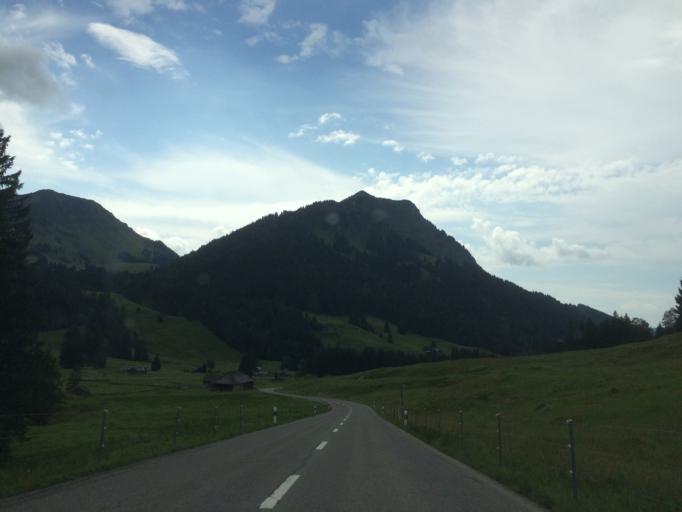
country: CH
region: Appenzell Ausserrhoden
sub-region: Bezirk Hinterland
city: Urnasch
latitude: 47.2446
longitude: 9.2753
